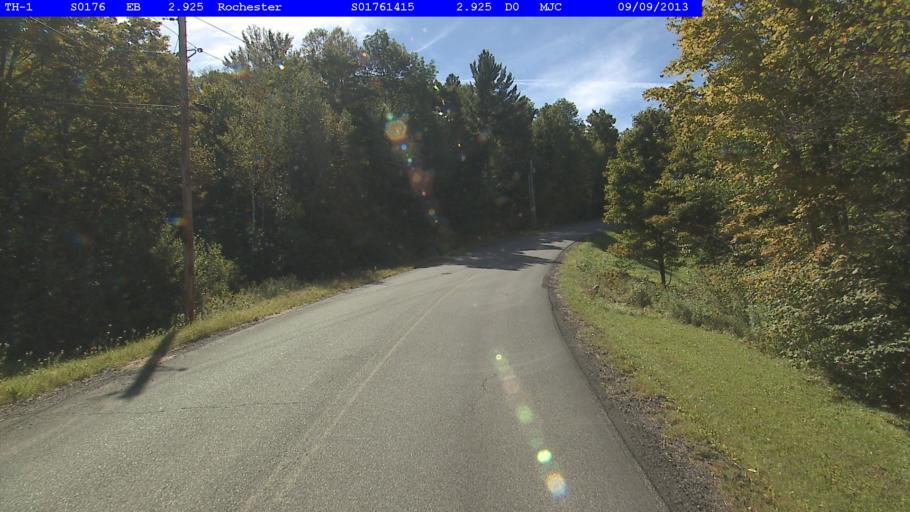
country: US
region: Vermont
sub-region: Orange County
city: Randolph
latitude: 43.8625
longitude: -72.7620
